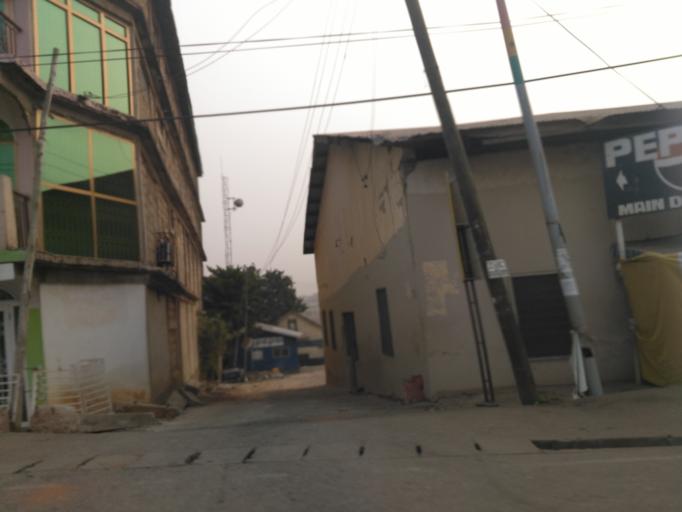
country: GH
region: Ashanti
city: Kumasi
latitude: 6.6858
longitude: -1.6174
